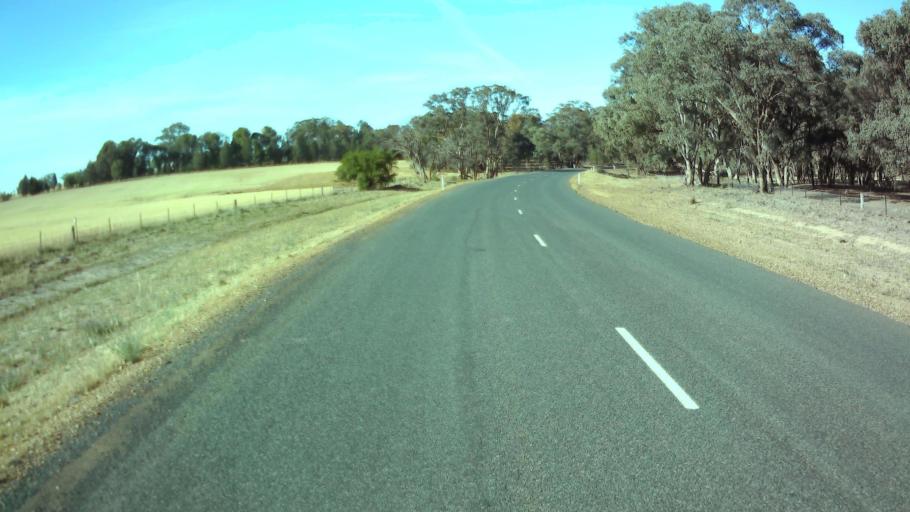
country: AU
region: New South Wales
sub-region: Weddin
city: Grenfell
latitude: -33.9878
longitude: 148.1401
